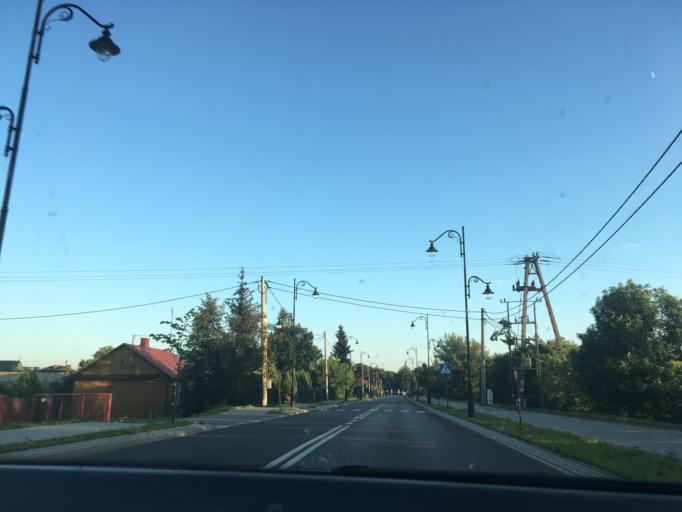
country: PL
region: Lublin Voivodeship
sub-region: Powiat radzynski
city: Radzyn Podlaski
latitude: 51.7903
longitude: 22.6241
